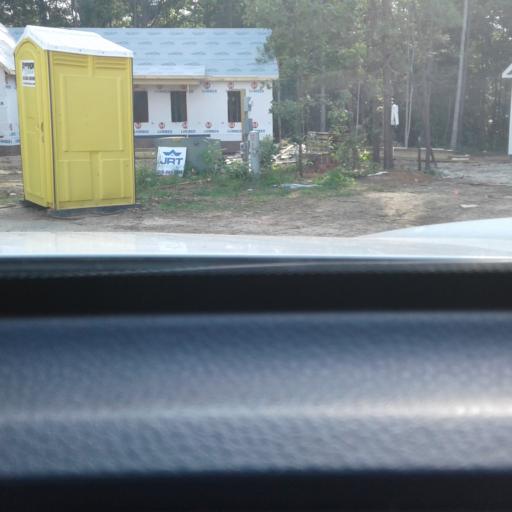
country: US
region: North Carolina
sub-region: Harnett County
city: Dunn
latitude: 35.3375
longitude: -78.5823
